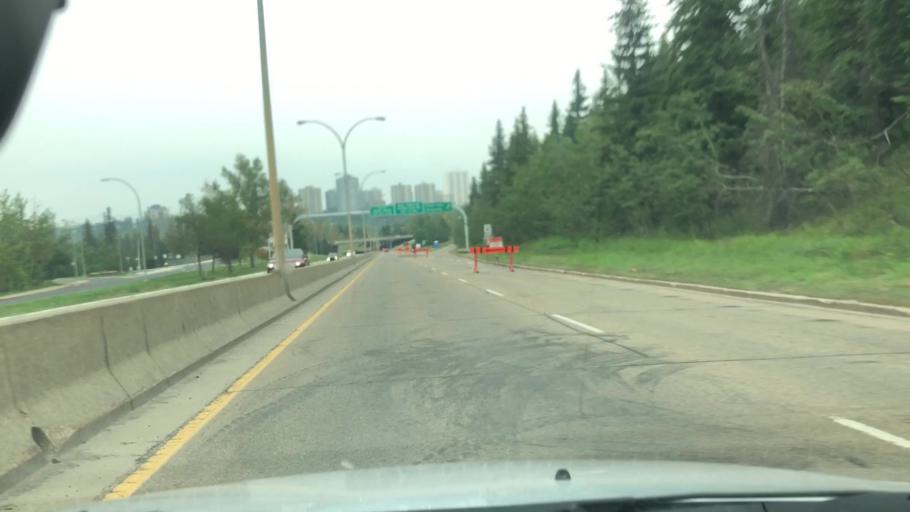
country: CA
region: Alberta
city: Edmonton
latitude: 53.5284
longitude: -113.5400
